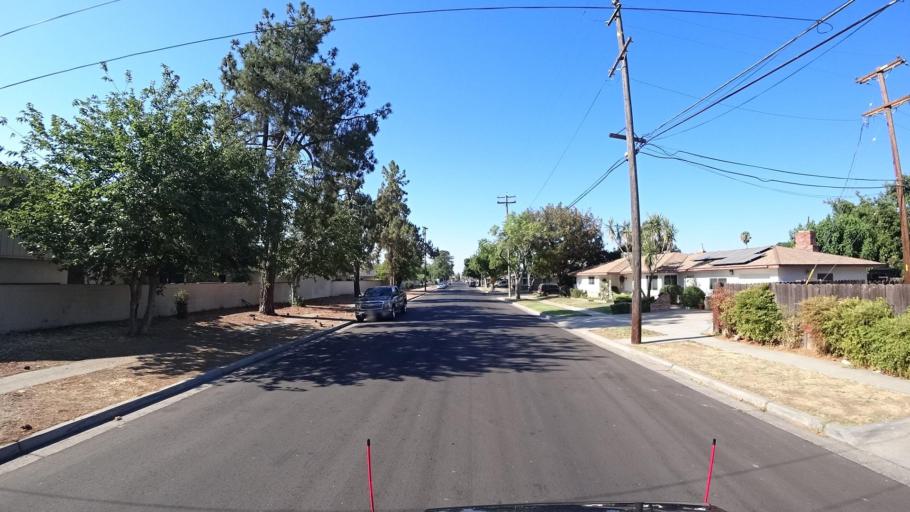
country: US
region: California
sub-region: Fresno County
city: Fresno
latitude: 36.7843
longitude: -119.7556
